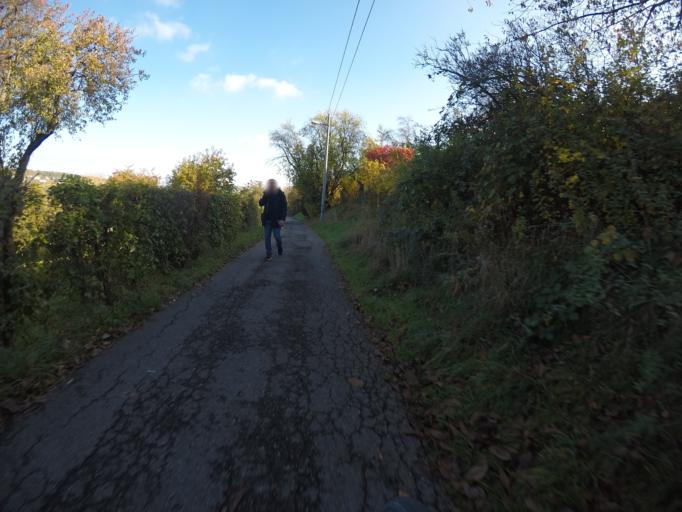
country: DE
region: Baden-Wuerttemberg
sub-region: Regierungsbezirk Stuttgart
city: Leinfelden-Echterdingen
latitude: 48.7396
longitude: 9.1209
